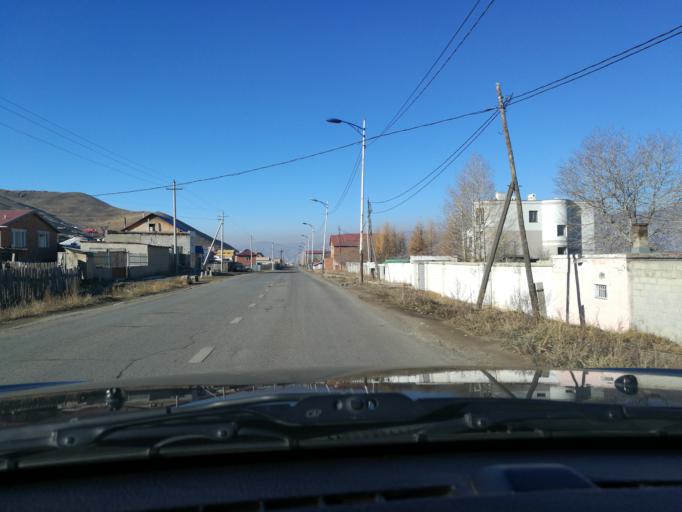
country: MN
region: Ulaanbaatar
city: Ulaanbaatar
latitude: 47.9801
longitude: 106.9466
